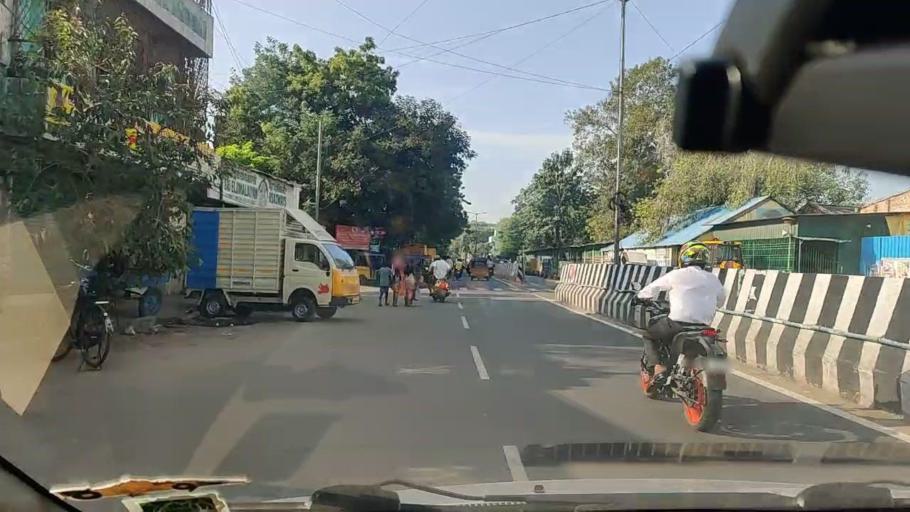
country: IN
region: Tamil Nadu
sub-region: Chennai
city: George Town
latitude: 13.0978
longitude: 80.2753
